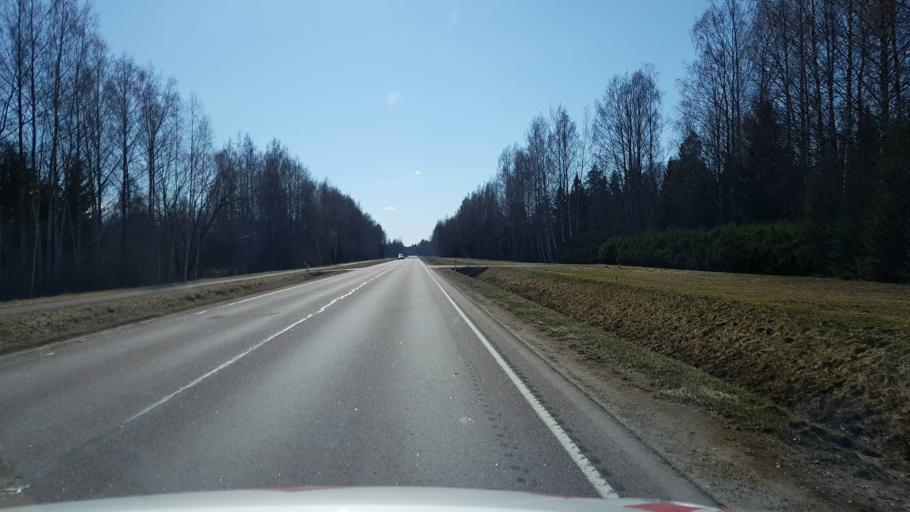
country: EE
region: Jogevamaa
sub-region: Mustvee linn
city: Mustvee
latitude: 58.7734
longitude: 26.9105
